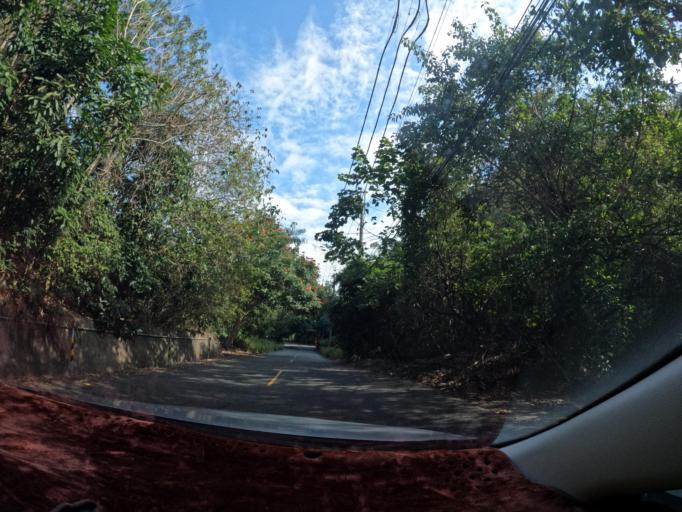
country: TW
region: Taiwan
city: Yujing
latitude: 23.0056
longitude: 120.3911
